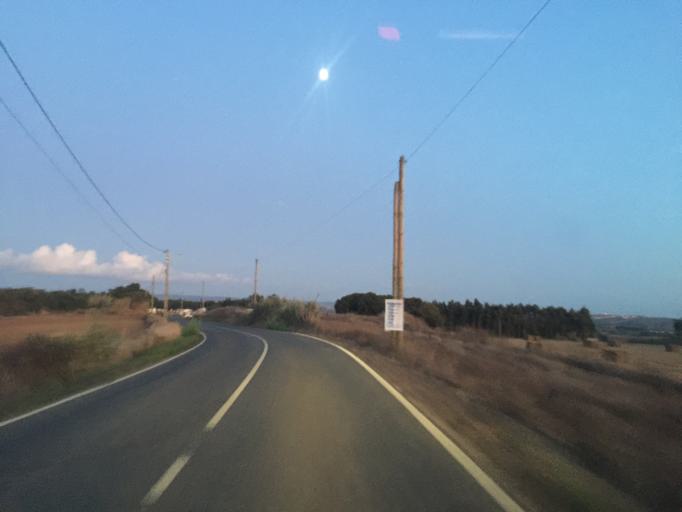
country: PT
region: Lisbon
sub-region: Lourinha
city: Lourinha
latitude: 39.2738
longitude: -9.2961
